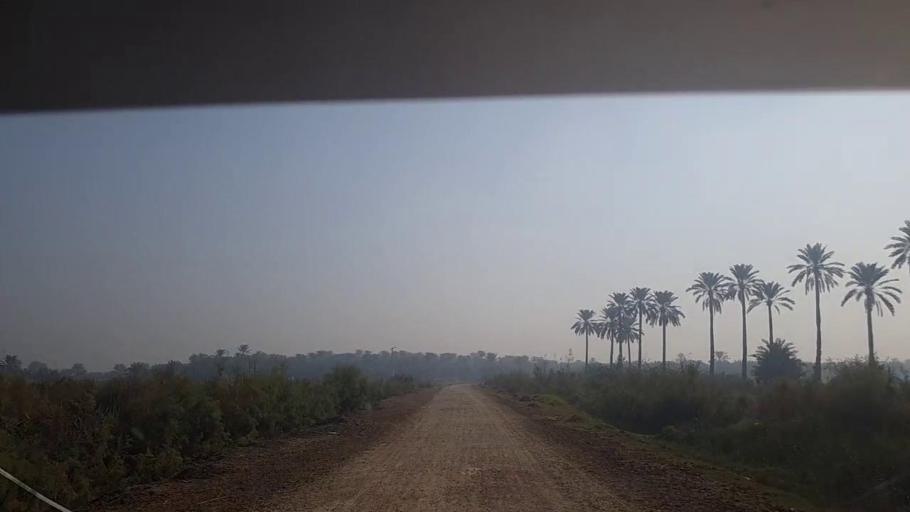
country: PK
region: Sindh
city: Khairpur
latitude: 27.4798
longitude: 68.7171
